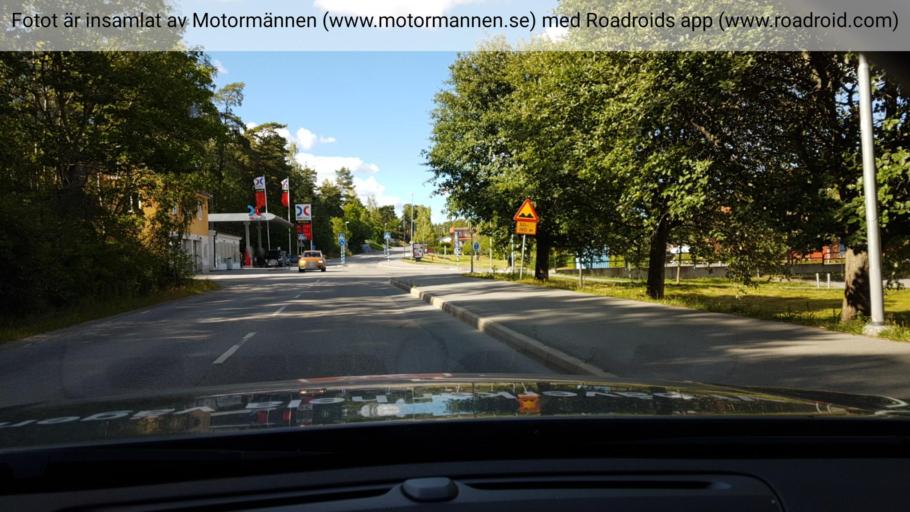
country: SE
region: Stockholm
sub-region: Sigtuna Kommun
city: Sigtuna
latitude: 59.6221
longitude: 17.7220
